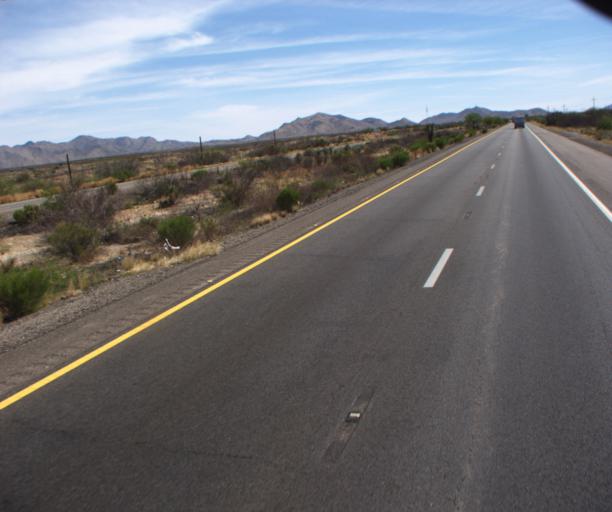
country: US
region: Arizona
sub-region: Cochise County
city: Saint David
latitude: 31.9835
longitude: -110.2035
